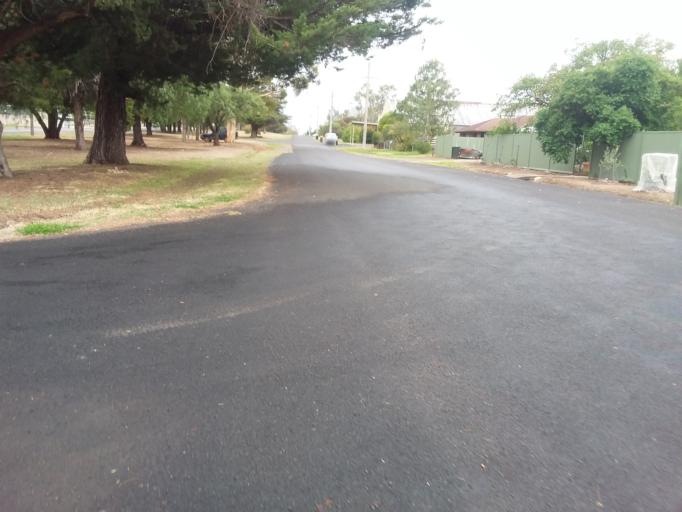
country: AU
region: Victoria
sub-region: Horsham
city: Horsham
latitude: -36.7423
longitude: 141.9399
